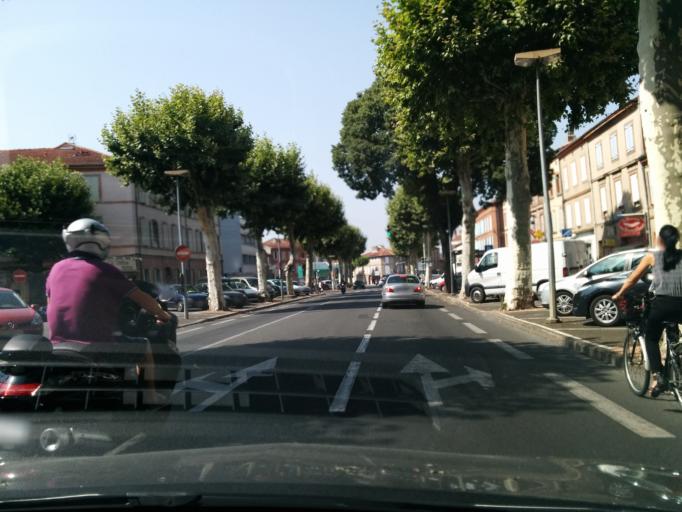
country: FR
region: Midi-Pyrenees
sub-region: Departement du Tarn
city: Albi
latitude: 43.9338
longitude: 2.1466
